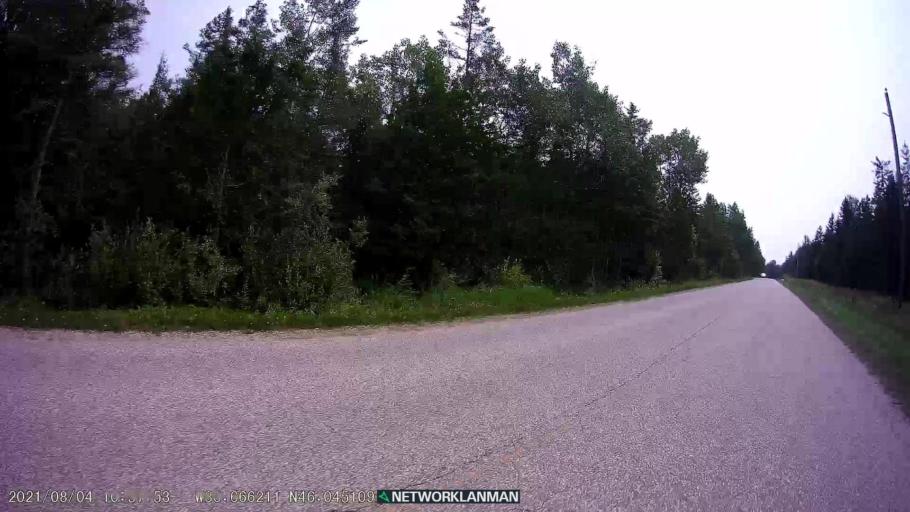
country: CA
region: Ontario
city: Thessalon
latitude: 46.0450
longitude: -83.6663
